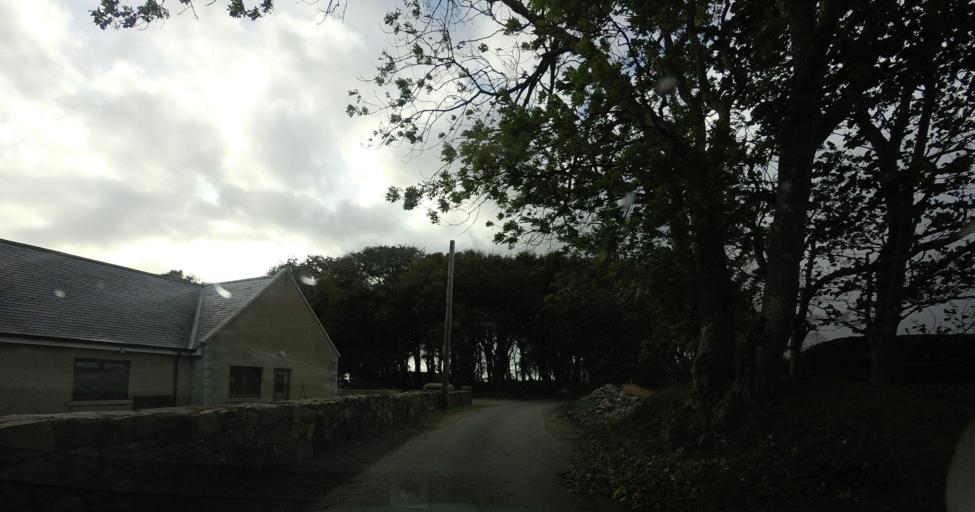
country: GB
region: Scotland
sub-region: Aberdeenshire
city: Whitehills
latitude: 57.6642
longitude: -2.6007
